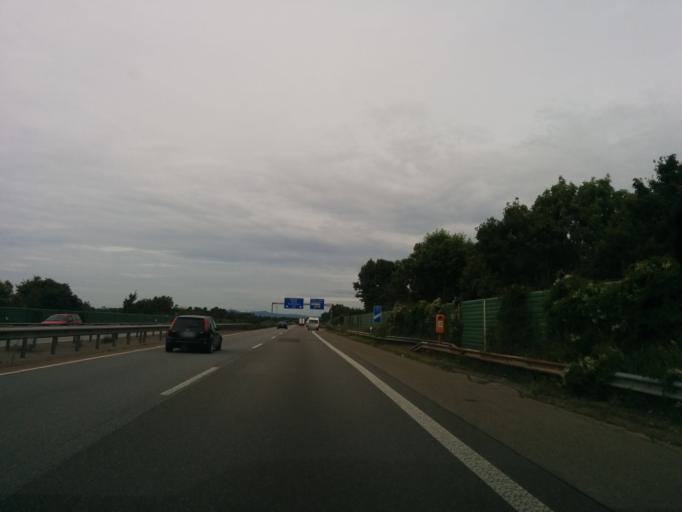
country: DE
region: Rheinland-Pfalz
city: Otterstadt
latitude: 49.3537
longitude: 8.4337
